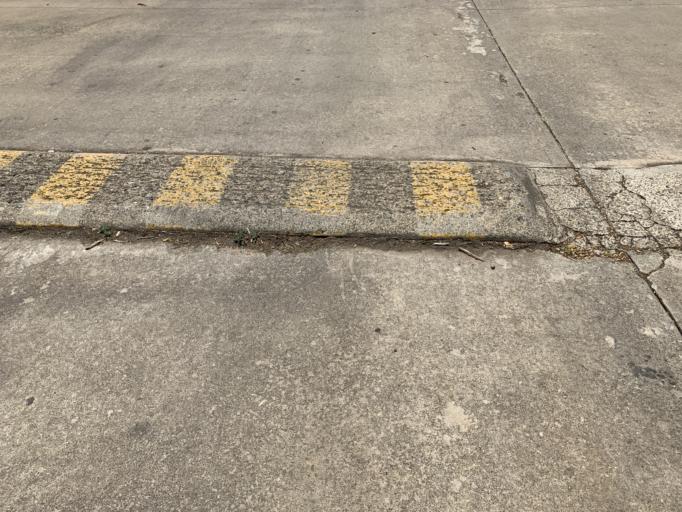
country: AU
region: New South Wales
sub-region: Holroyd
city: Girraween
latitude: -33.7738
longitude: 150.9514
